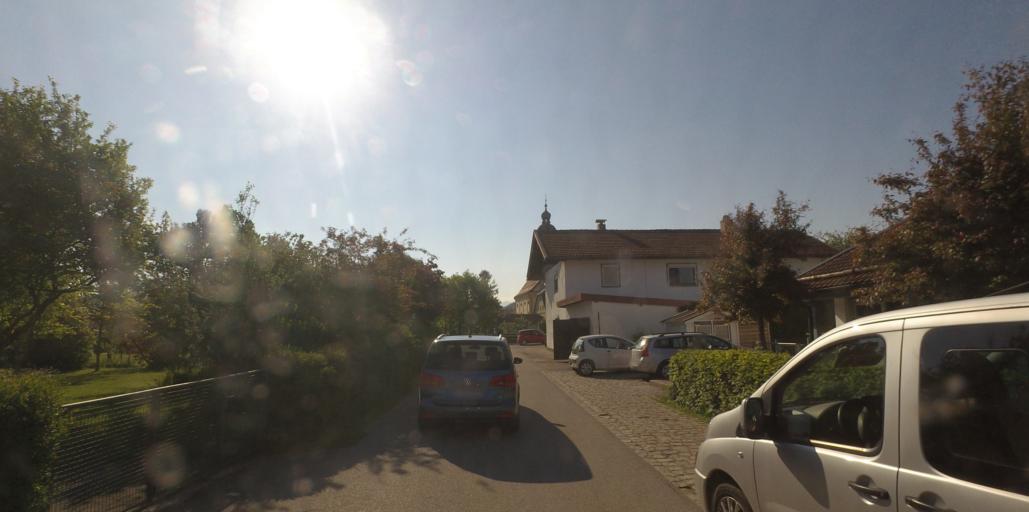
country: DE
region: Bavaria
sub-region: Upper Bavaria
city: Vachendorf
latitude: 47.8431
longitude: 12.6045
